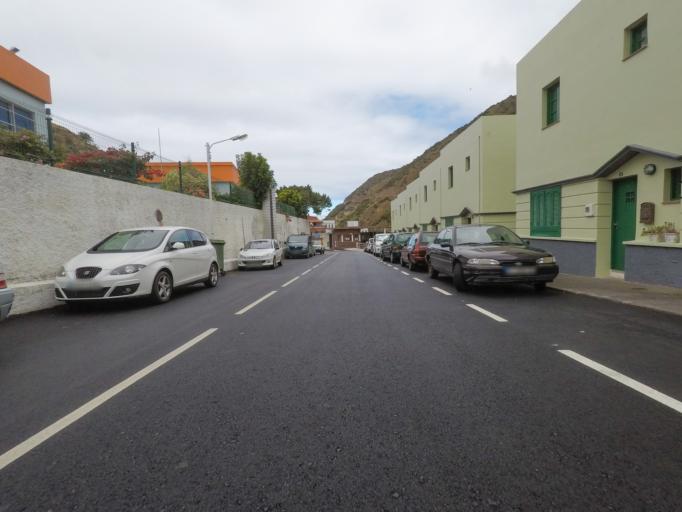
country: ES
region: Canary Islands
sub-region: Provincia de Santa Cruz de Tenerife
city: Vallehermosa
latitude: 28.1809
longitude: -17.2648
